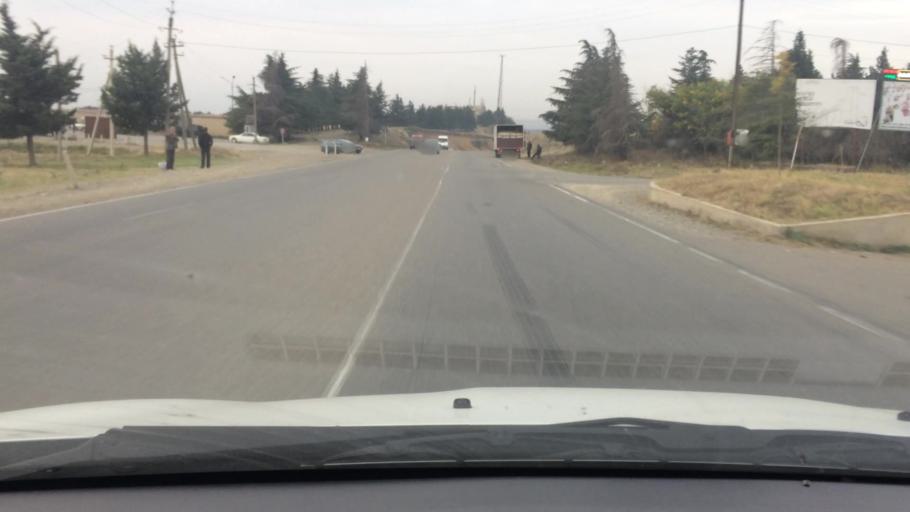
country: GE
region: T'bilisi
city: Tbilisi
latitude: 41.6278
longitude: 44.8073
